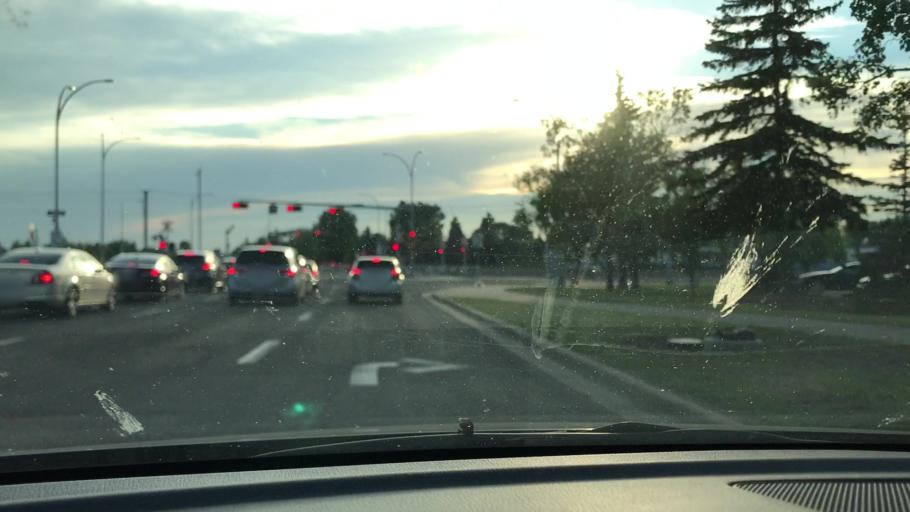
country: CA
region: Alberta
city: Edmonton
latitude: 53.4833
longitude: -113.5152
